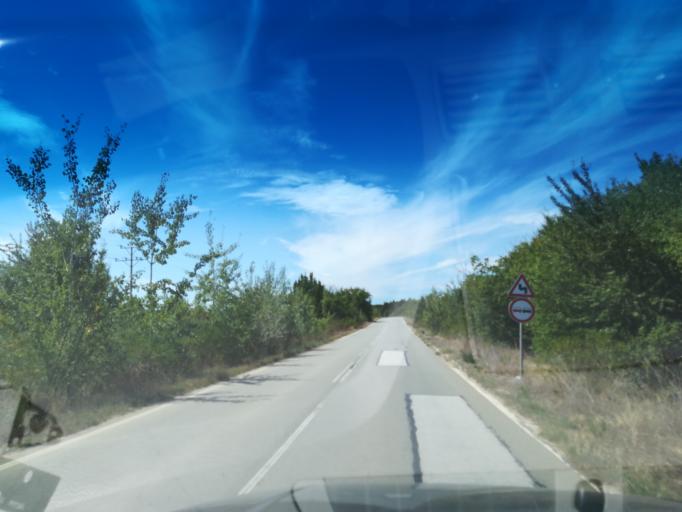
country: BG
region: Plovdiv
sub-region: Obshtina Suedinenie
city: Suedinenie
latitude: 42.3994
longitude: 24.5461
